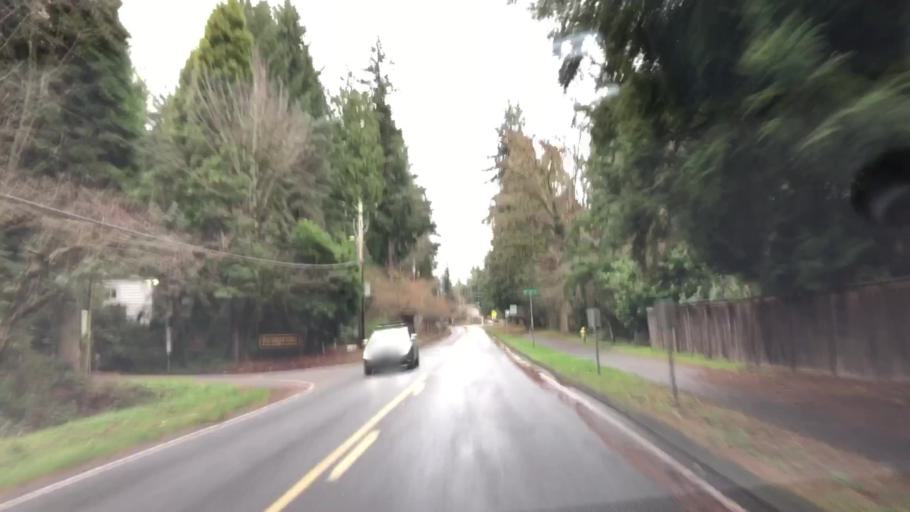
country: US
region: Washington
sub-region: King County
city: Woodinville
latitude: 47.7667
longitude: -122.1648
